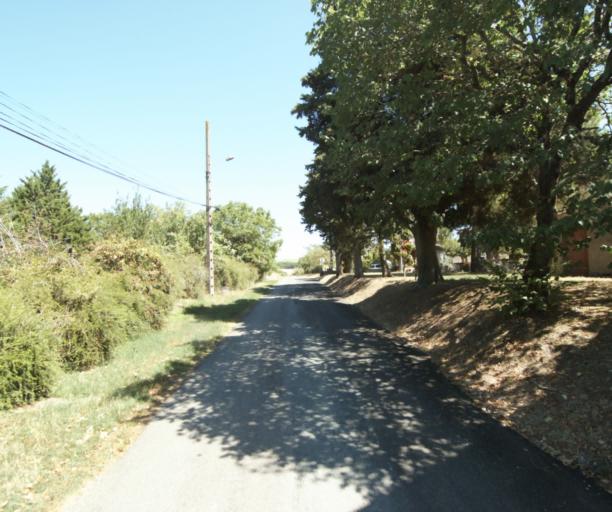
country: FR
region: Midi-Pyrenees
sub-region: Departement de la Haute-Garonne
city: Saint-Felix-Lauragais
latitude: 43.4933
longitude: 1.9284
